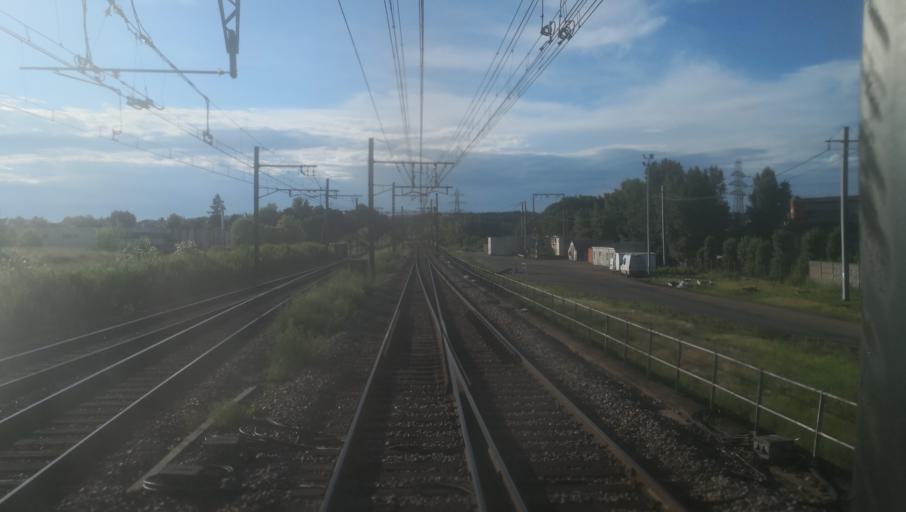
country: FR
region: Centre
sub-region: Departement du Cher
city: Vierzon
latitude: 47.2113
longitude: 2.0982
